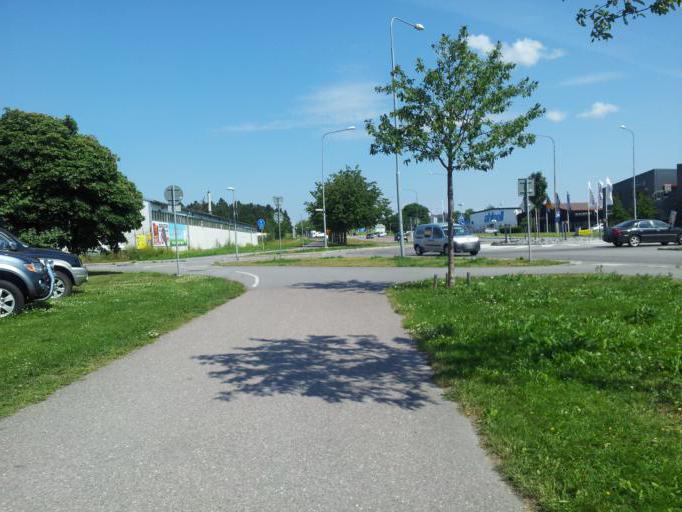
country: SE
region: Uppsala
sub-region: Uppsala Kommun
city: Saevja
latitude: 59.8473
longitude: 17.6779
